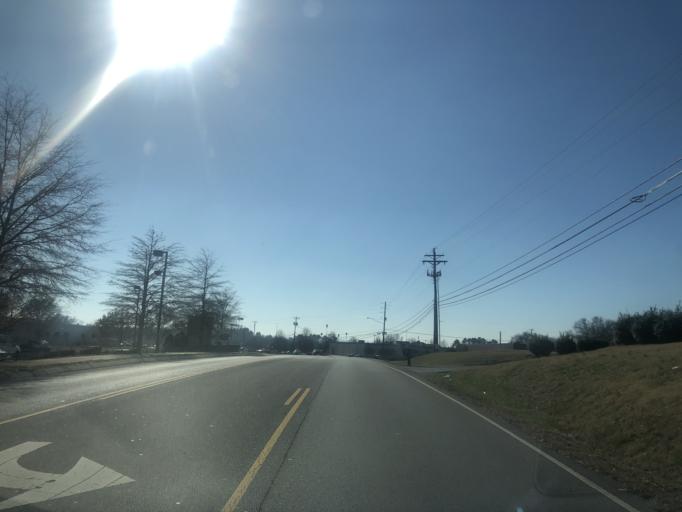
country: US
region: Tennessee
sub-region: Rutherford County
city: Smyrna
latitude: 35.9415
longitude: -86.5289
